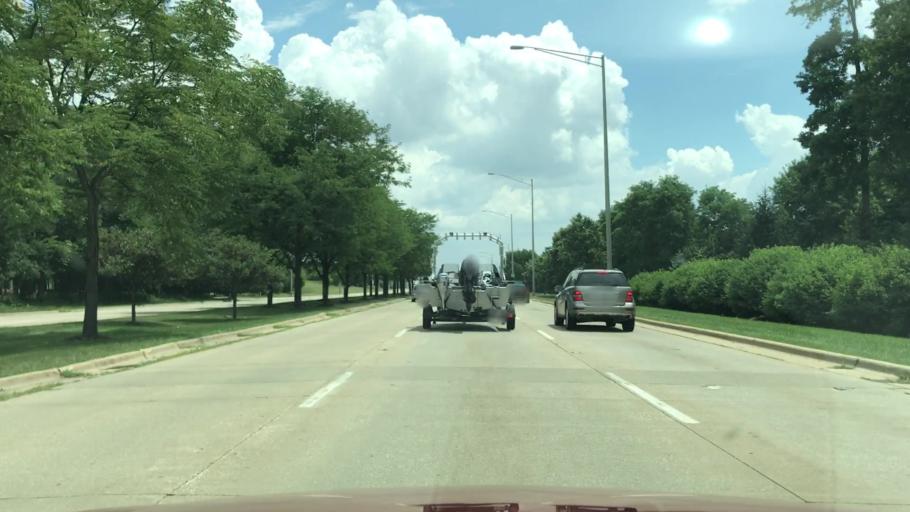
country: US
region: Illinois
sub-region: DuPage County
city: Bloomingdale
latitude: 41.9553
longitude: -88.0549
